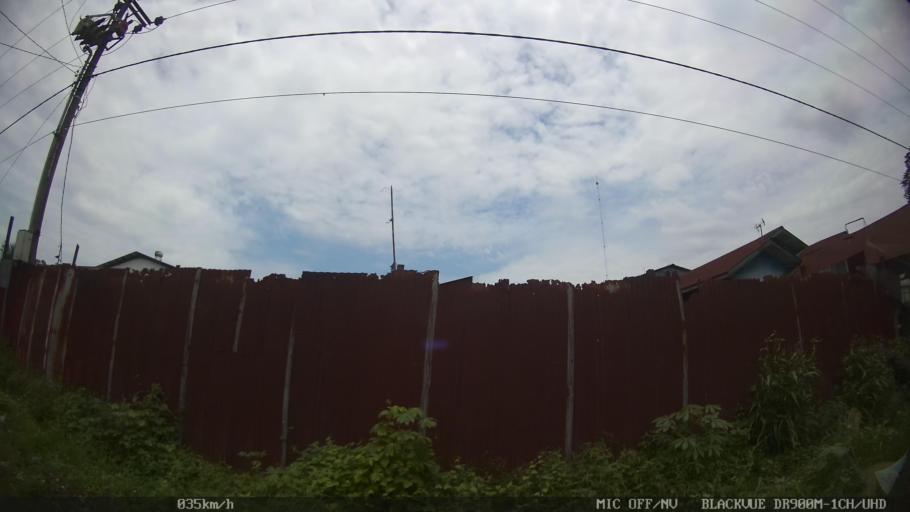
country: ID
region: North Sumatra
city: Sunggal
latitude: 3.6140
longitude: 98.5804
